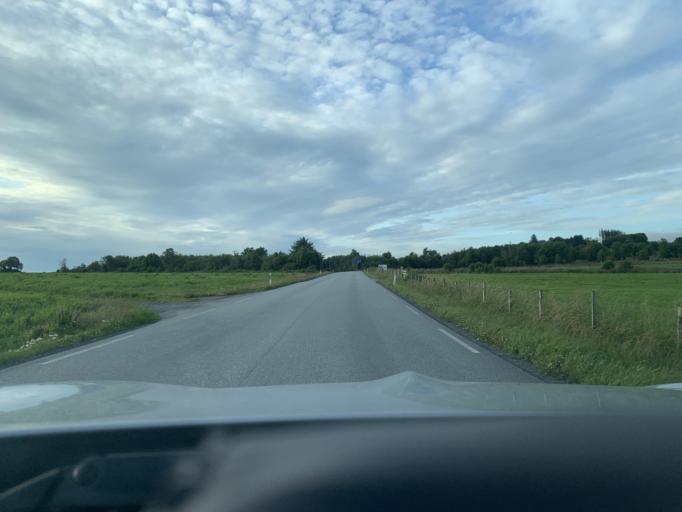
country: NO
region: Rogaland
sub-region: Time
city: Bryne
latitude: 58.6959
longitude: 5.7101
